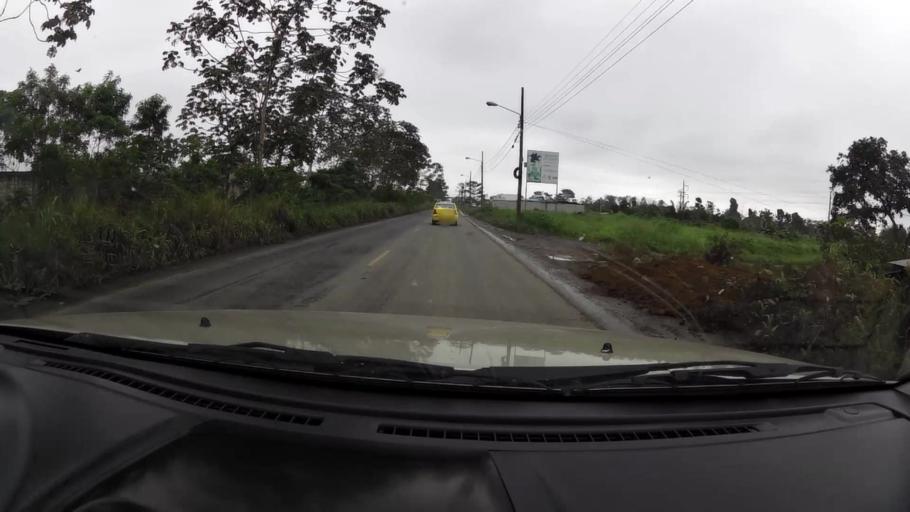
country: EC
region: Guayas
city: Balao
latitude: -3.0709
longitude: -79.7513
